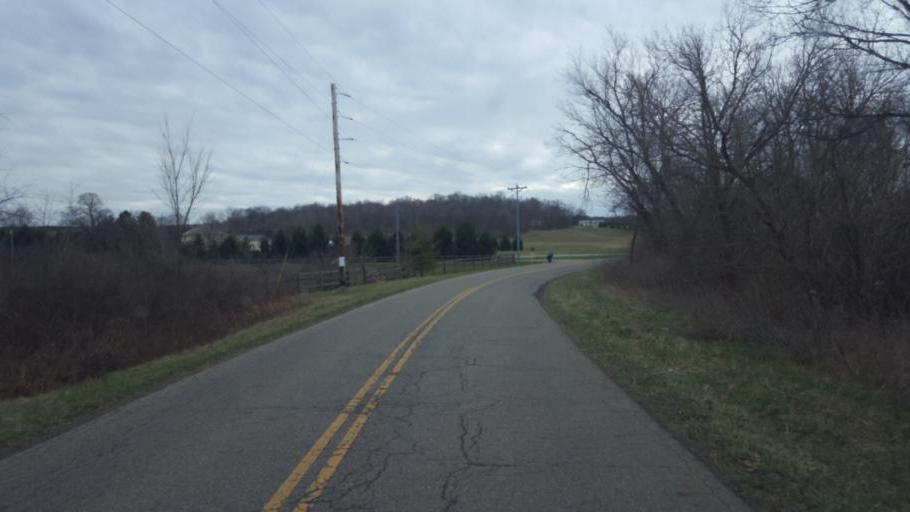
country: US
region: Ohio
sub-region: Knox County
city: Fredericktown
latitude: 40.5181
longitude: -82.4833
